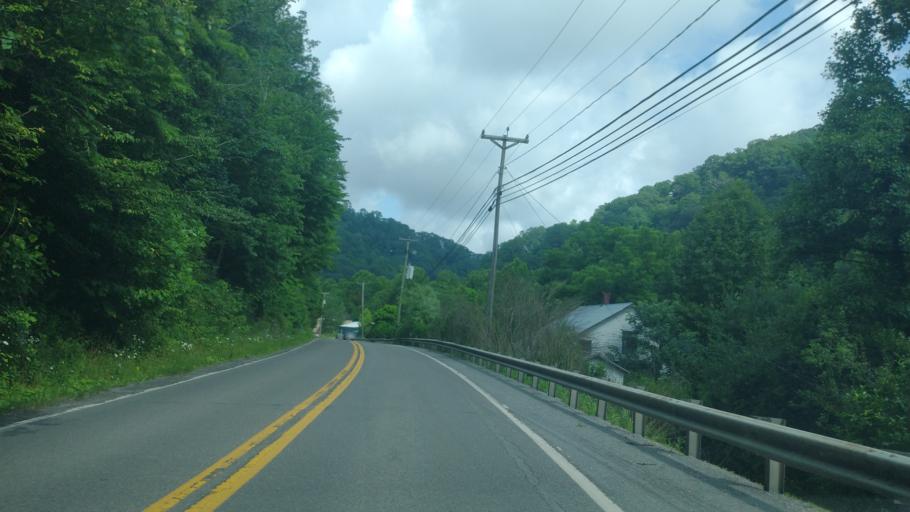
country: US
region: West Virginia
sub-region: McDowell County
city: Welch
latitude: 37.4041
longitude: -81.4203
